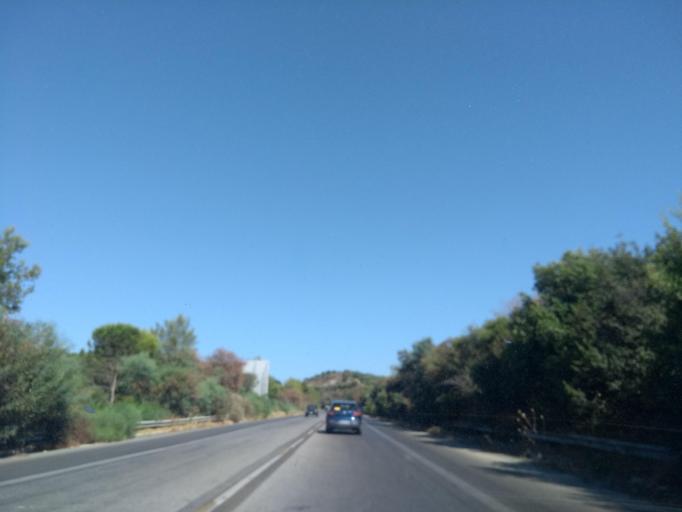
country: GR
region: Crete
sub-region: Nomos Chanias
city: Gerani
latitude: 35.5155
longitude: 23.8278
